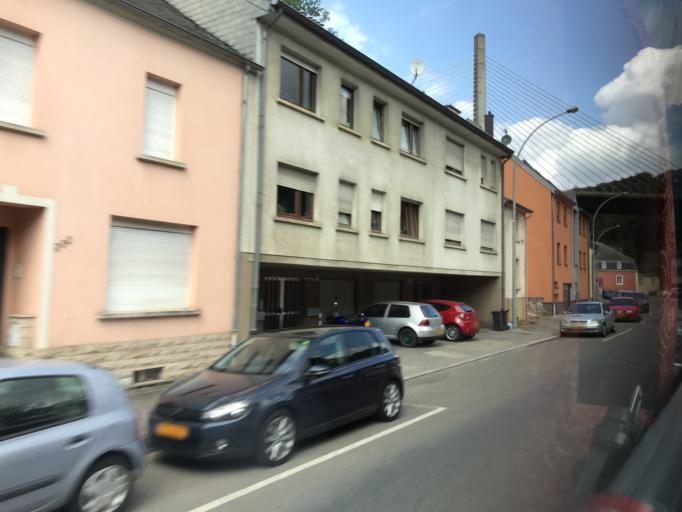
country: LU
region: Luxembourg
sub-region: Canton de Luxembourg
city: Hesperange
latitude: 49.5773
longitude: 6.1538
